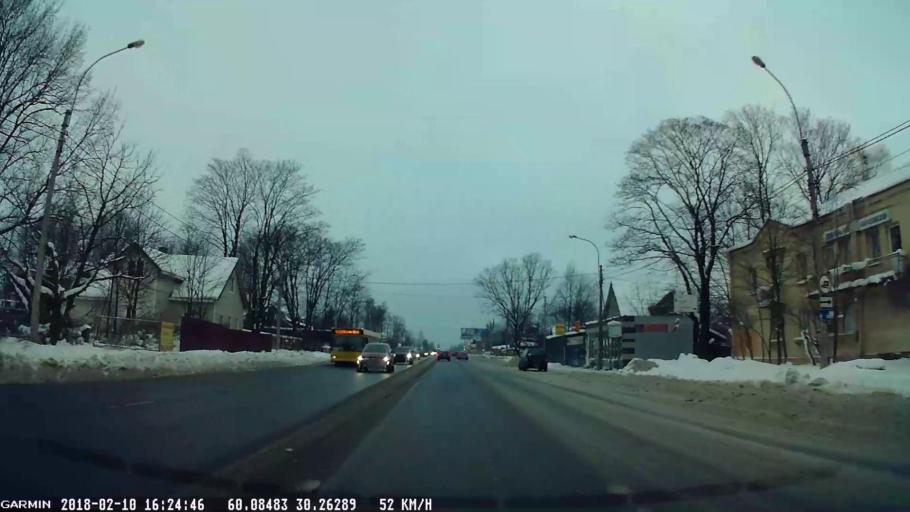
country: RU
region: St.-Petersburg
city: Pargolovo
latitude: 60.0856
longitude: 30.2623
